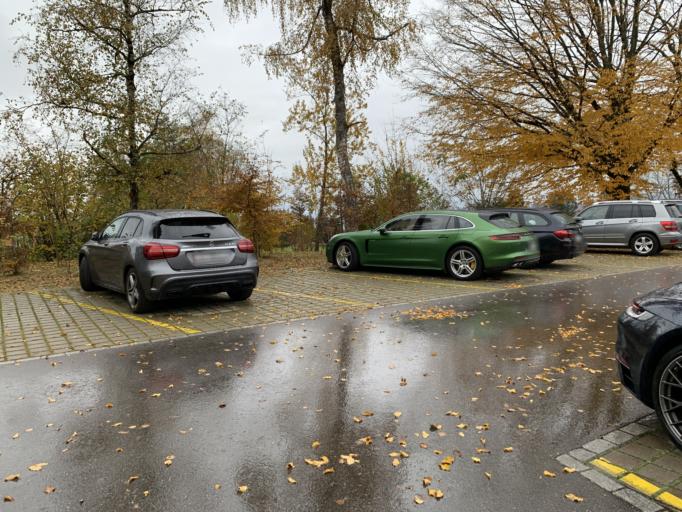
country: CH
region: Zurich
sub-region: Bezirk Pfaeffikon
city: Hittnau / Hittnau (Dorf)
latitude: 47.3609
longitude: 8.8446
